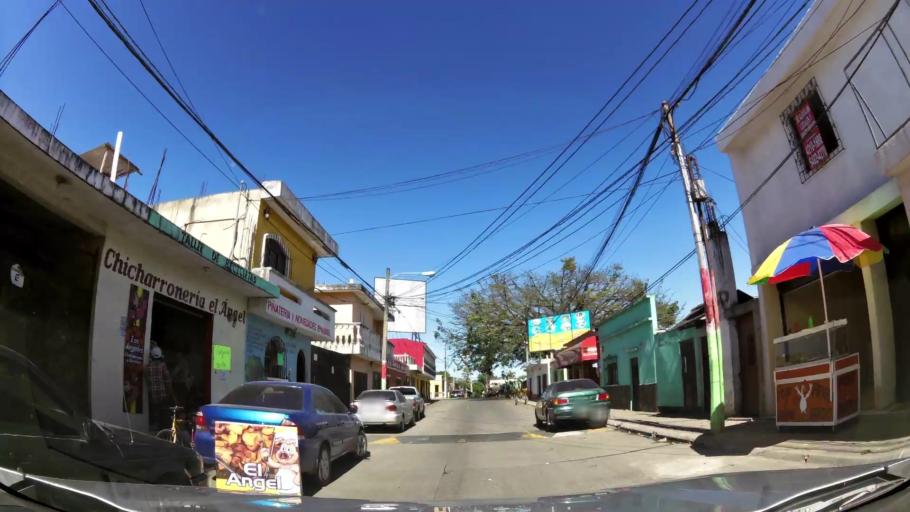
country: GT
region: Guatemala
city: Petapa
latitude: 14.4980
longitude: -90.5565
